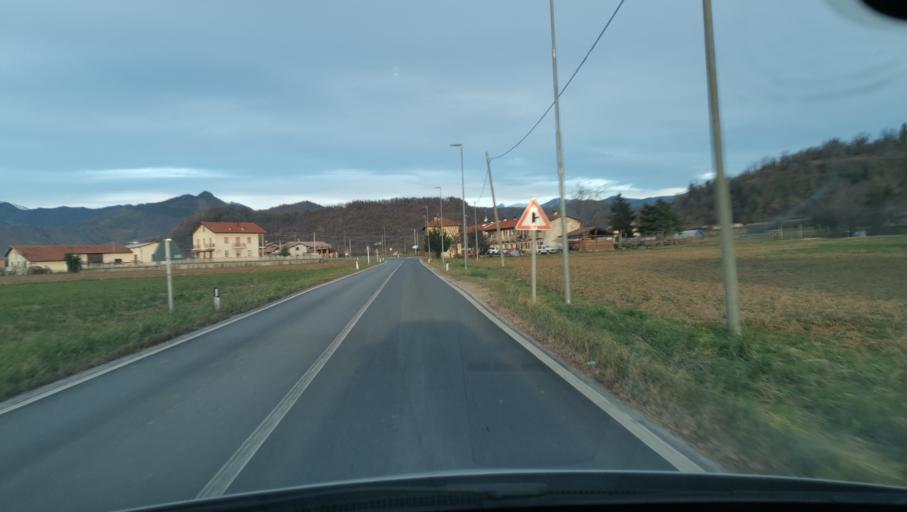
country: IT
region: Piedmont
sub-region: Provincia di Cuneo
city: Caraglio
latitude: 44.4142
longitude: 7.4208
